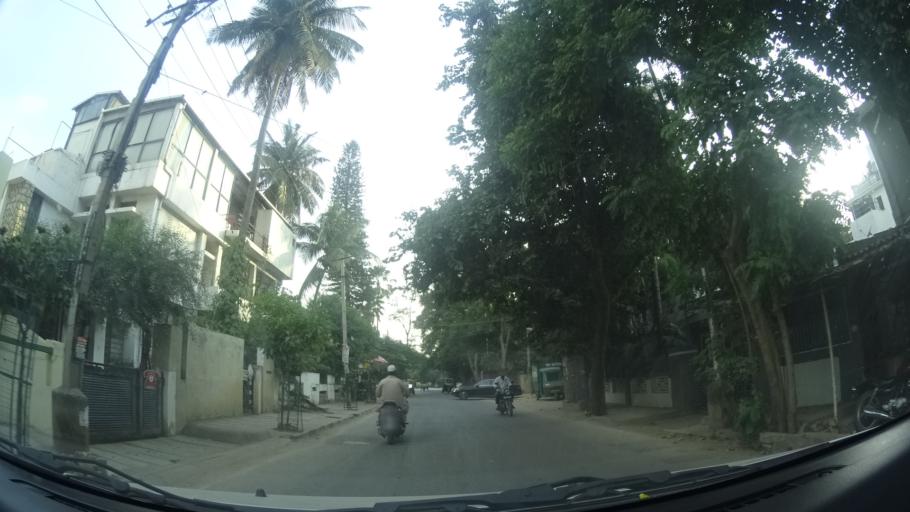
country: IN
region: Karnataka
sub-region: Bangalore Urban
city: Bangalore
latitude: 13.0027
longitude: 77.6252
